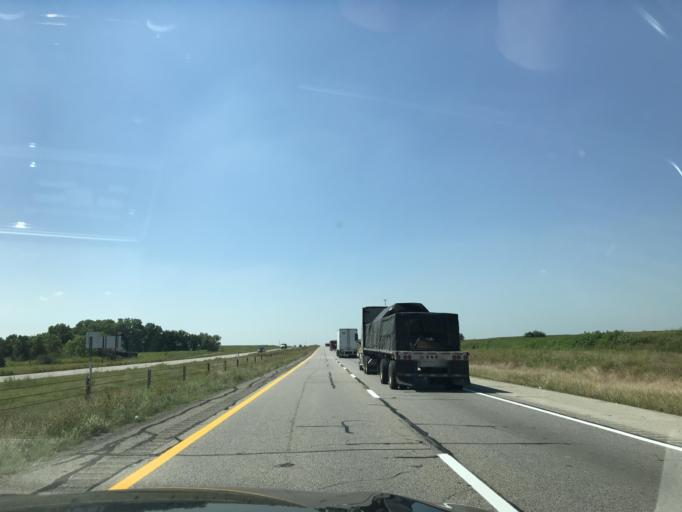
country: US
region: Texas
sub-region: Johnson County
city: Grandview
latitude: 32.3374
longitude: -97.1914
